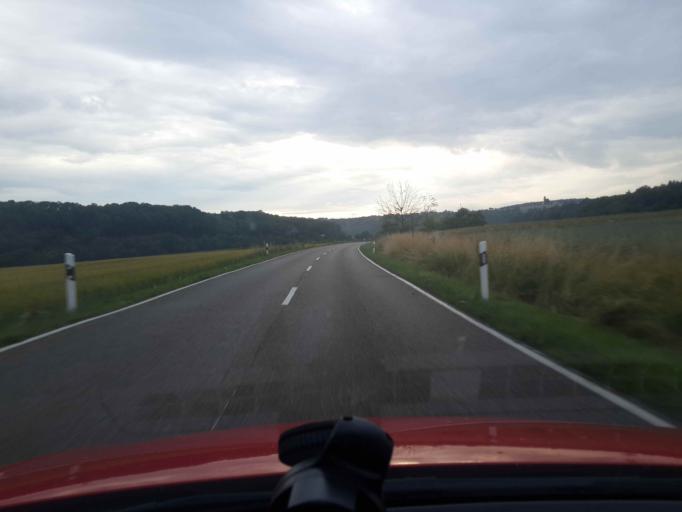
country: DE
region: Baden-Wuerttemberg
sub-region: Regierungsbezirk Stuttgart
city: Neudenau
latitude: 49.2715
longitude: 9.2476
